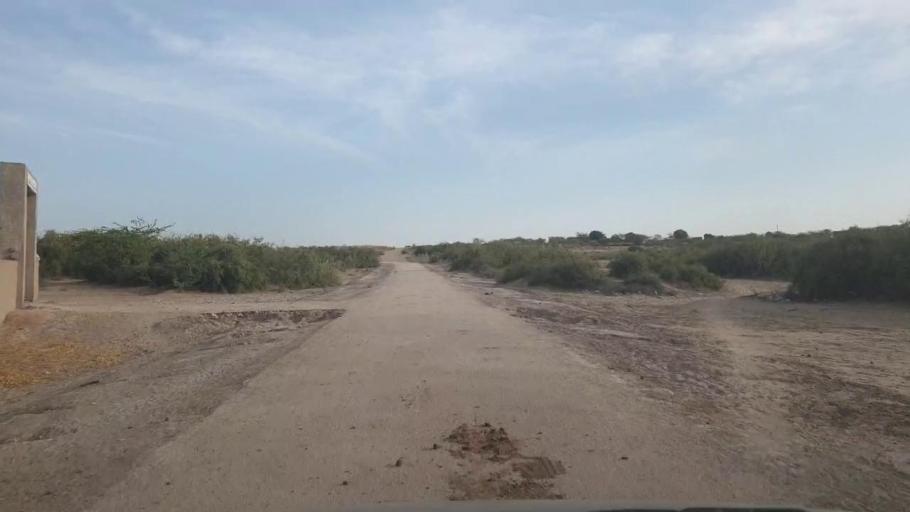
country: PK
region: Sindh
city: Nabisar
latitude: 25.0650
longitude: 69.6452
